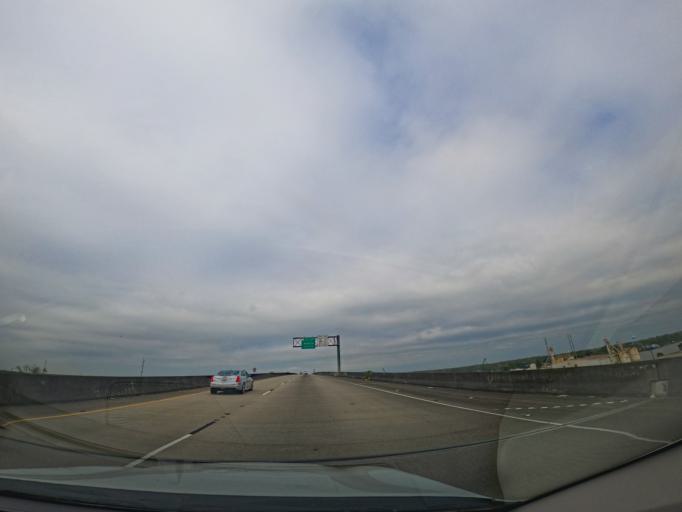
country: US
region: Louisiana
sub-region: Saint Mary Parish
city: Amelia
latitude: 29.6705
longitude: -91.0960
